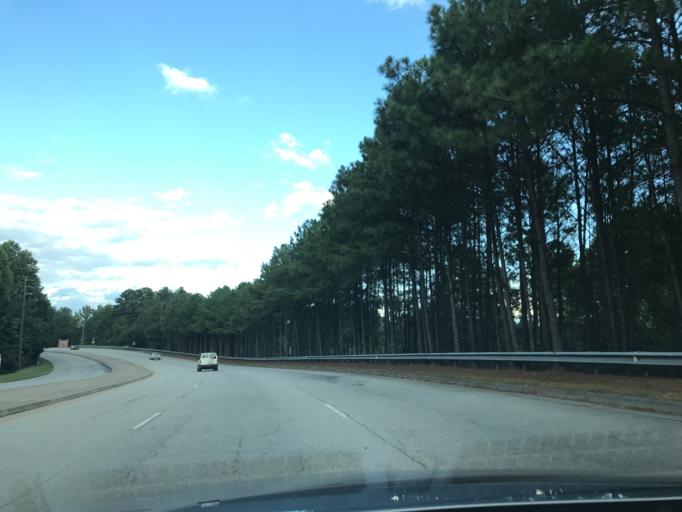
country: US
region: Georgia
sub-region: Douglas County
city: Douglasville
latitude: 33.7362
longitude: -84.7361
